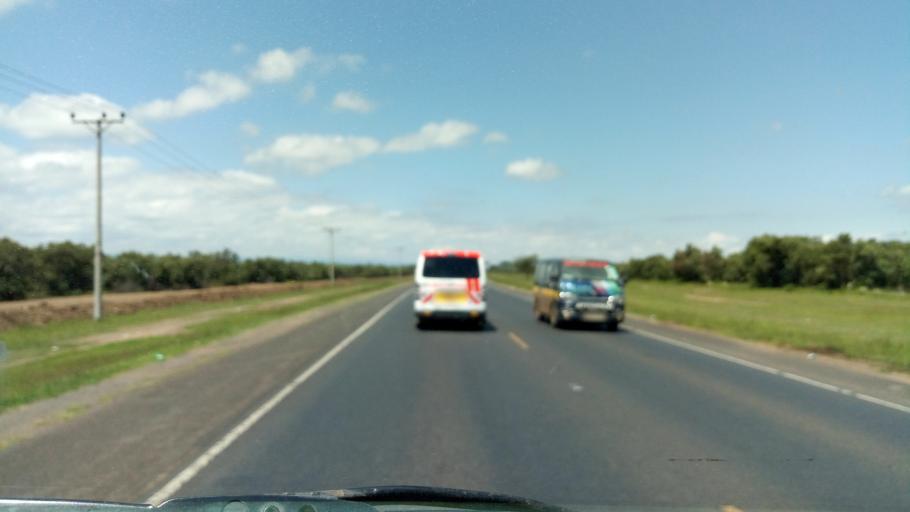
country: KE
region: Nakuru
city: Naivasha
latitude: -0.5540
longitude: 36.3494
